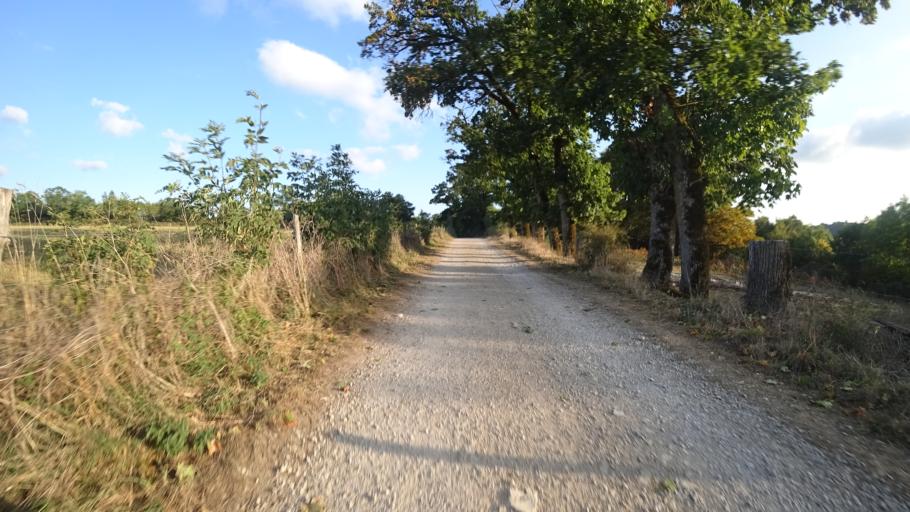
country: FR
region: Midi-Pyrenees
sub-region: Departement de l'Aveyron
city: Sebazac-Concoures
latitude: 44.3911
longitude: 2.5868
